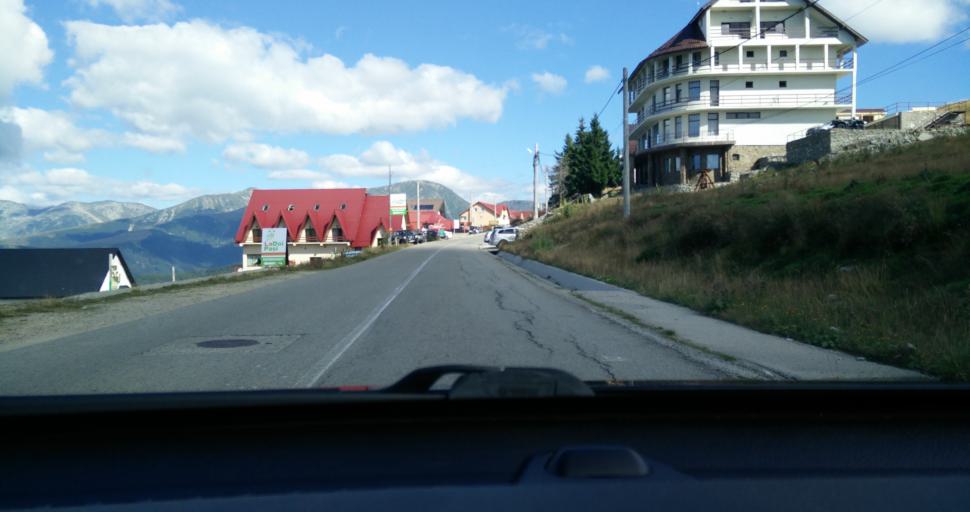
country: RO
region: Gorj
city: Novaci-Straini
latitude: 45.2766
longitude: 23.6896
